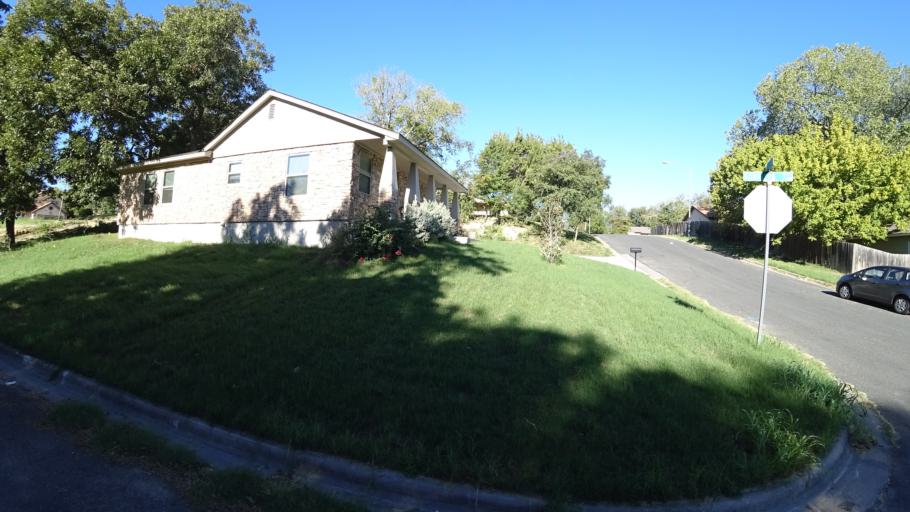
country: US
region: Texas
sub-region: Travis County
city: Hornsby Bend
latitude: 30.3094
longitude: -97.6532
